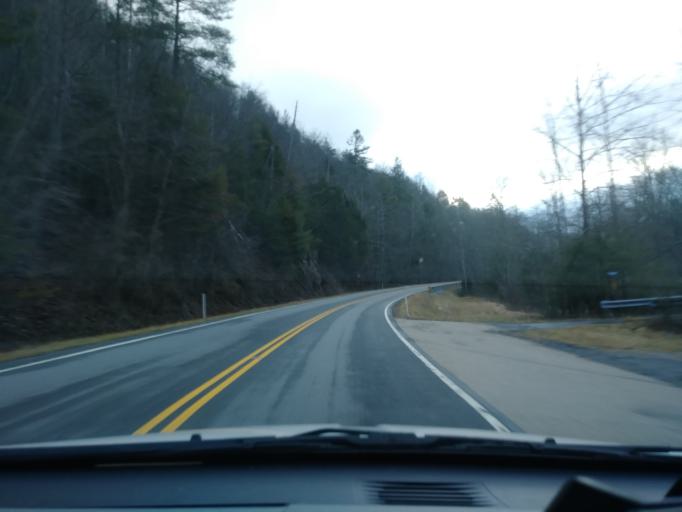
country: US
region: Tennessee
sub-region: Unicoi County
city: Unicoi
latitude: 36.1768
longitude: -82.3159
